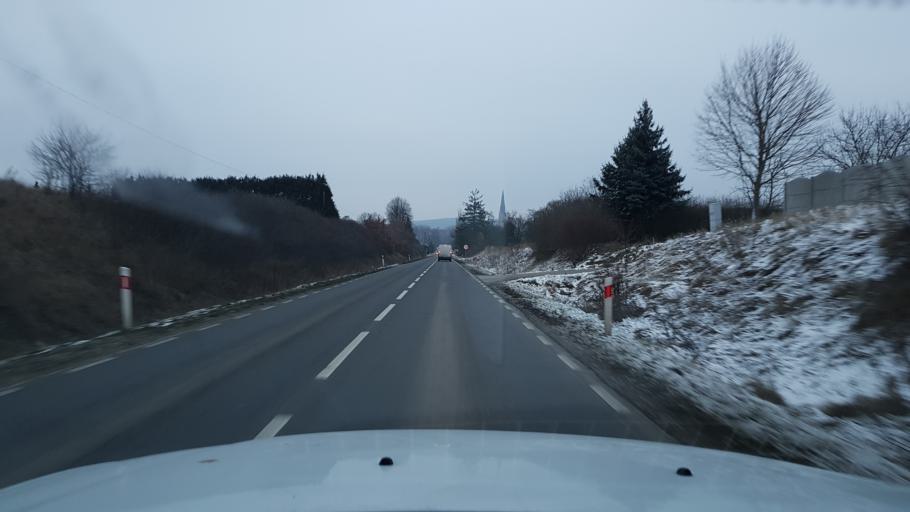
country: PL
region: West Pomeranian Voivodeship
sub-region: Powiat gryfinski
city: Chojna
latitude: 52.9559
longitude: 14.4141
